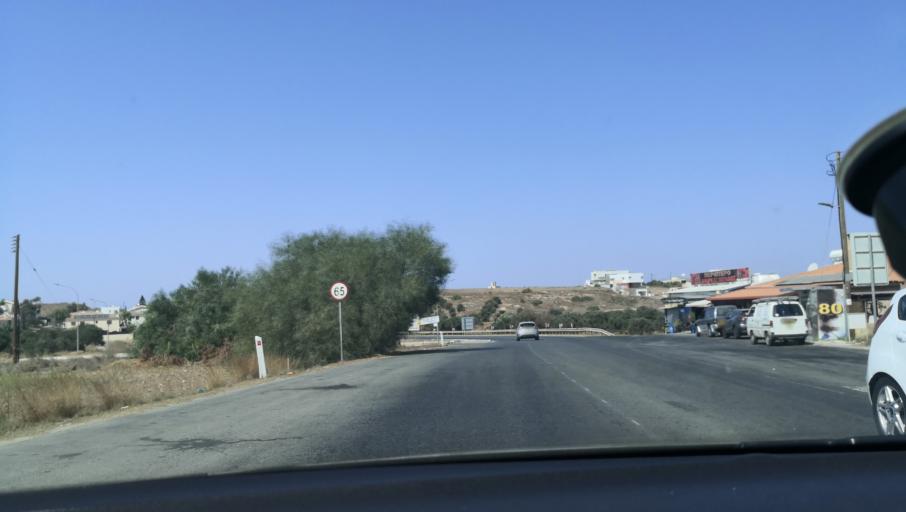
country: CY
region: Lefkosia
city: Kato Deftera
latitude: 35.1150
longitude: 33.2839
